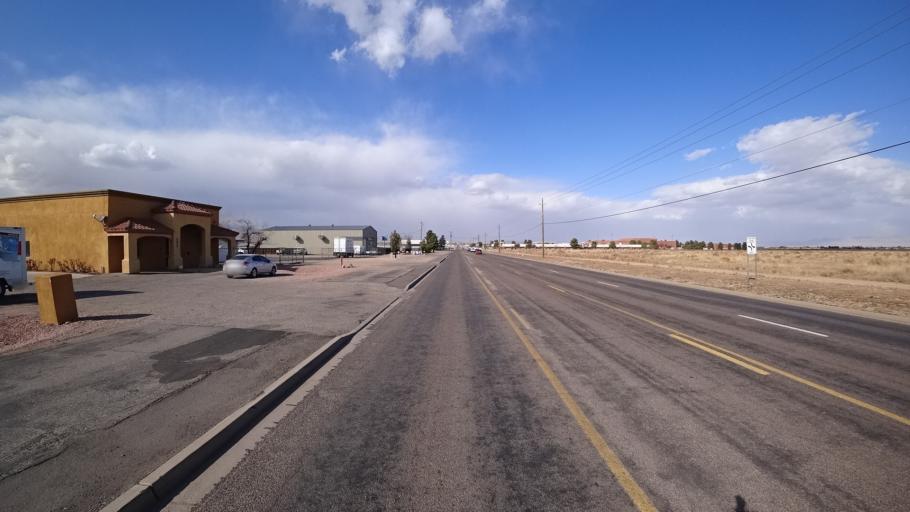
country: US
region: Arizona
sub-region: Mohave County
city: New Kingman-Butler
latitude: 35.2403
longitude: -114.0116
